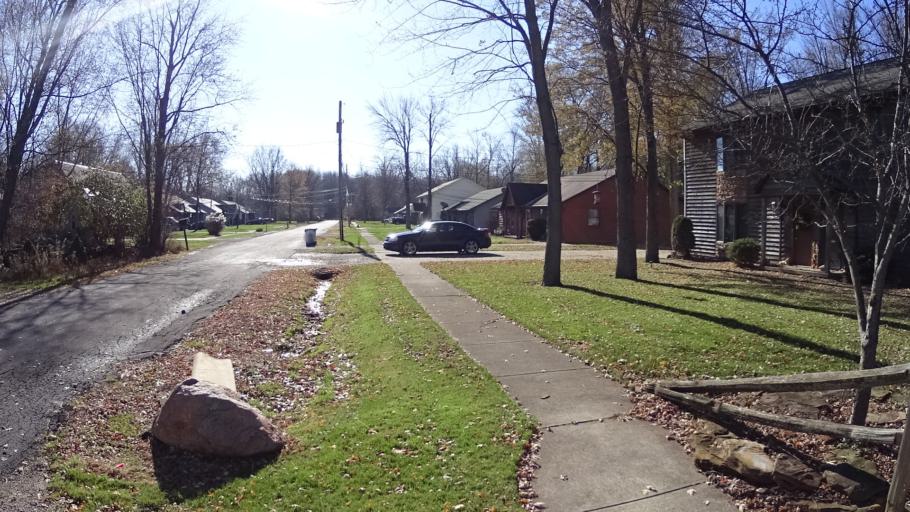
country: US
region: Ohio
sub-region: Lorain County
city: Sheffield Lake
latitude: 41.4959
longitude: -82.0765
